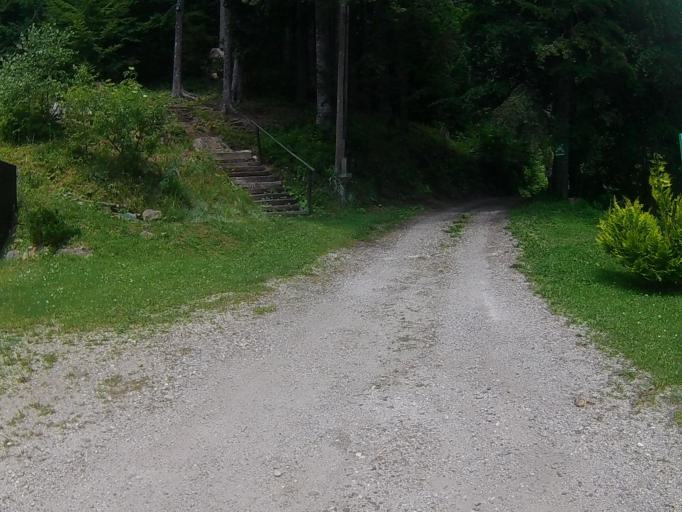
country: SI
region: Ruse
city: Bistrica ob Dravi
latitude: 46.5042
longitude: 15.5631
